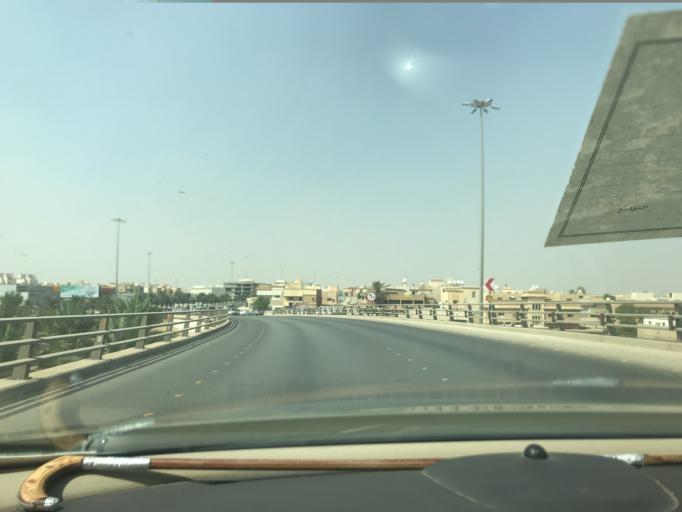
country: SA
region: Ar Riyad
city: Riyadh
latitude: 24.7159
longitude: 46.7628
